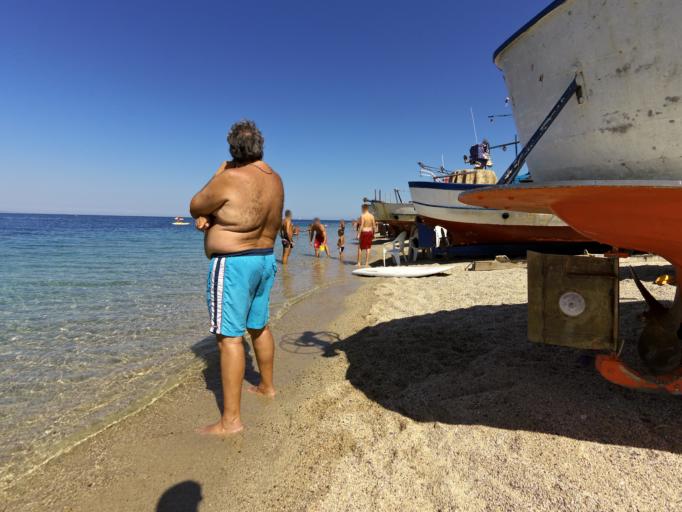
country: IT
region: Calabria
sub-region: Provincia di Catanzaro
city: Soverato Marina
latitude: 38.6917
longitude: 16.5495
